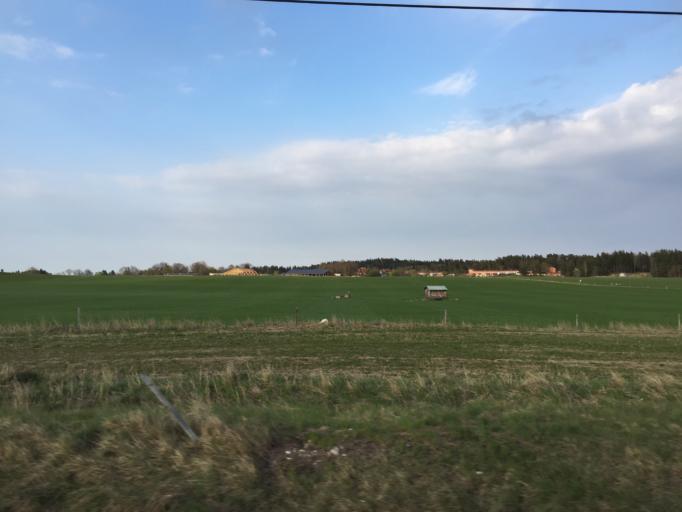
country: SE
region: Stockholm
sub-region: Sodertalje Kommun
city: Pershagen
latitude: 59.0600
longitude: 17.6127
